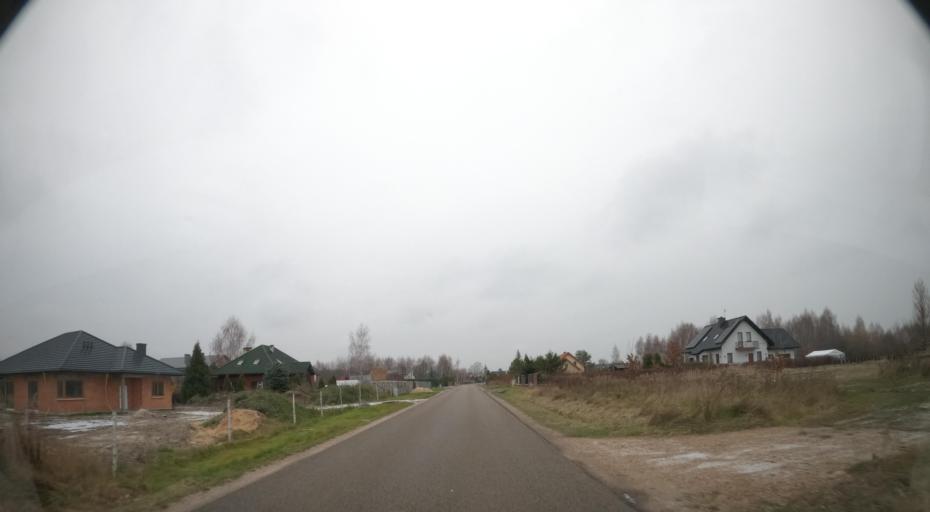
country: PL
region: Masovian Voivodeship
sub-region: Powiat radomski
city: Skaryszew
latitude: 51.3792
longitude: 21.2400
